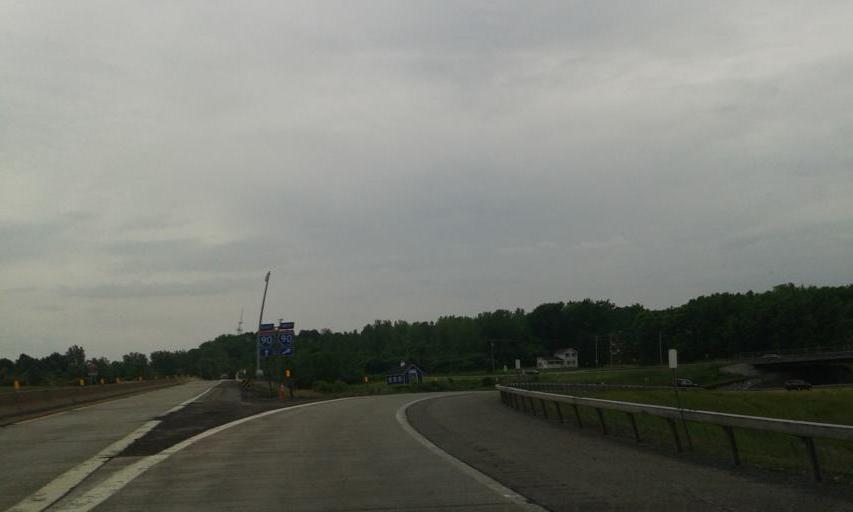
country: US
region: New York
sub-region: Onondaga County
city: Seneca Knolls
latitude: 43.1088
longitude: -76.2881
